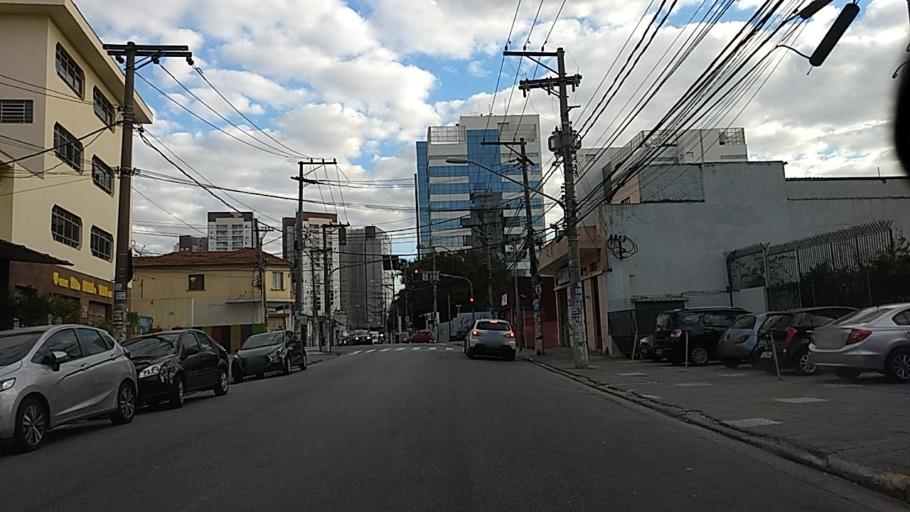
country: BR
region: Sao Paulo
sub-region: Sao Paulo
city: Sao Paulo
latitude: -23.4973
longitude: -46.6110
